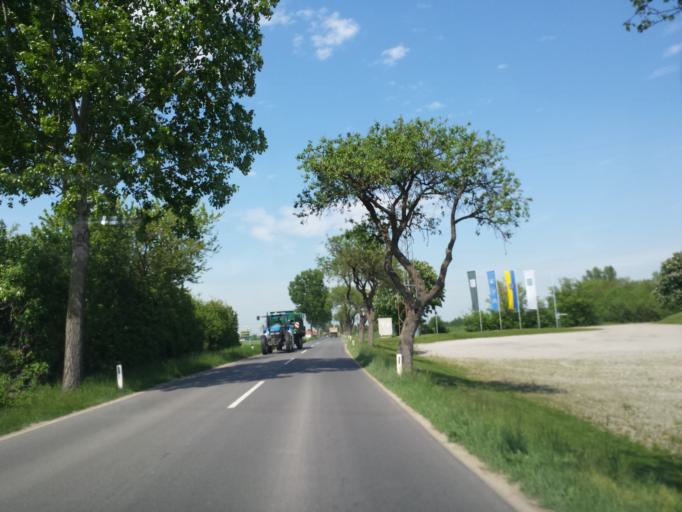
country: AT
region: Lower Austria
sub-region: Politischer Bezirk Tulln
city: Atzenbrugg
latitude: 48.3141
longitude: 15.9015
